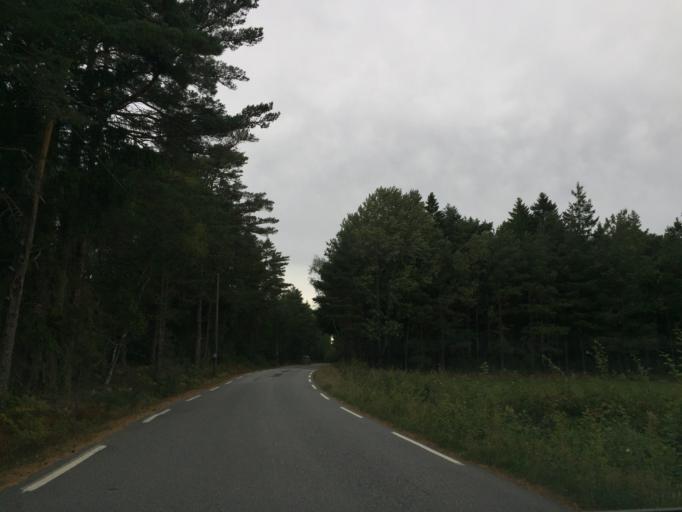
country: NO
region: Ostfold
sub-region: Hvaler
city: Skjaerhalden
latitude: 59.0729
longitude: 11.0246
